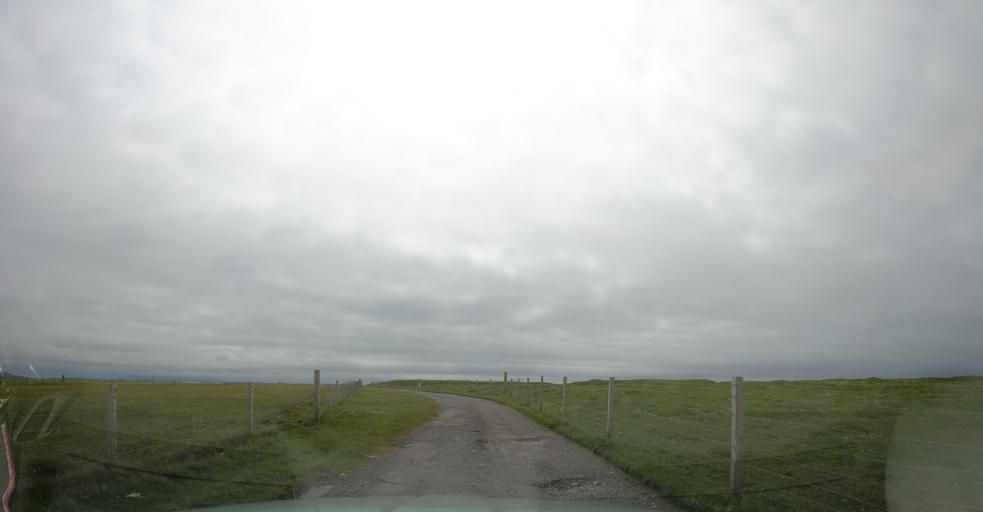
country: GB
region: Scotland
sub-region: Eilean Siar
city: Isle of North Uist
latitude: 57.5295
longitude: -7.3818
